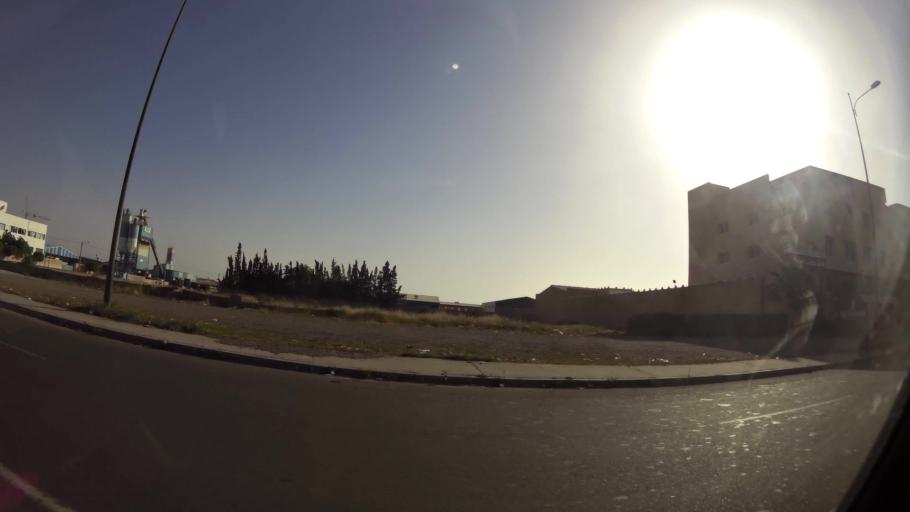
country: MA
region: Oued ed Dahab-Lagouira
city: Dakhla
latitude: 30.3930
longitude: -9.5324
